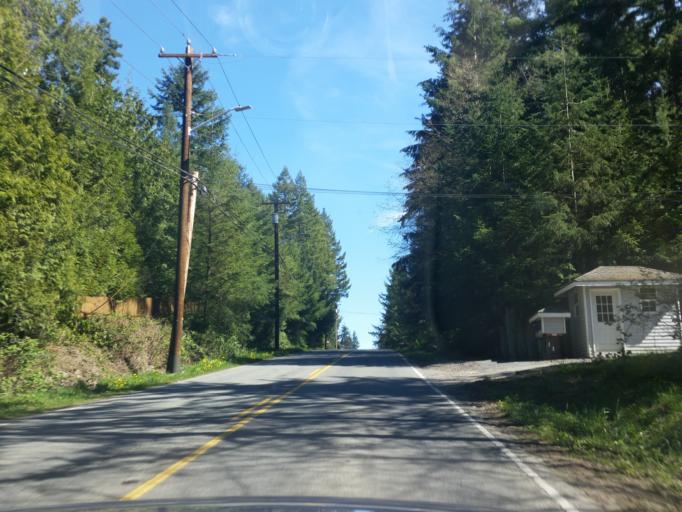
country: US
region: Washington
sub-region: Snohomish County
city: North Creek
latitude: 47.8342
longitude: -122.1583
